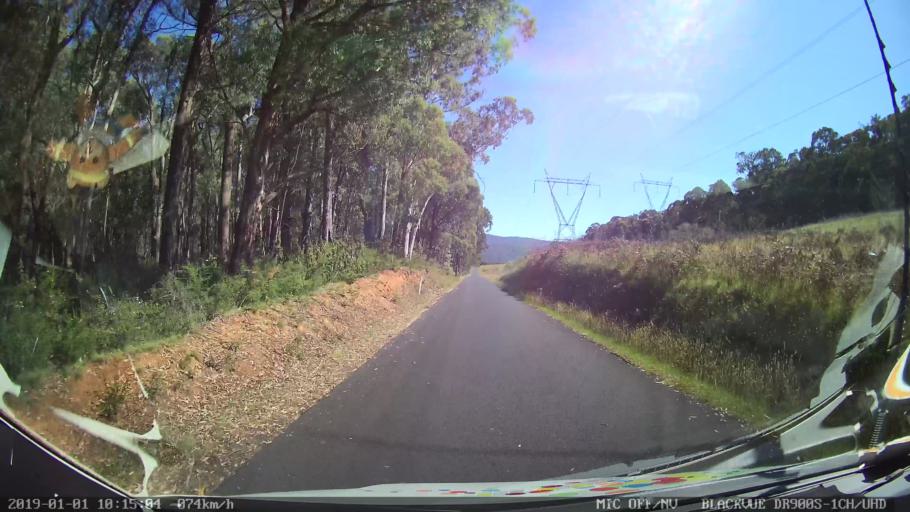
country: AU
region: New South Wales
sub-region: Snowy River
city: Jindabyne
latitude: -36.1057
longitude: 148.1617
